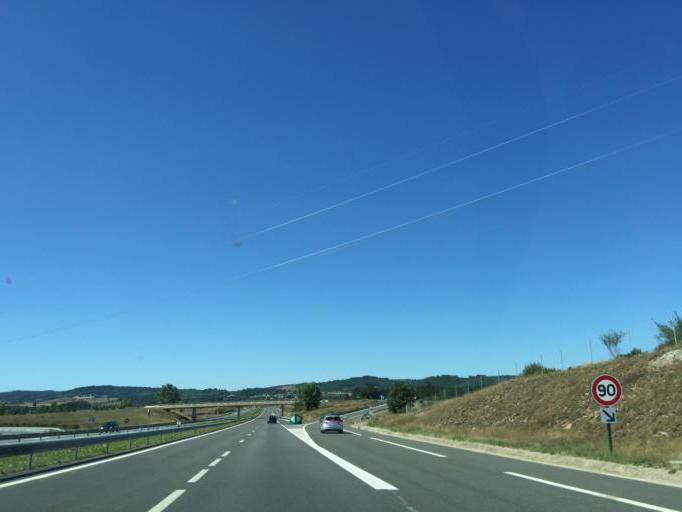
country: FR
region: Midi-Pyrenees
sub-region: Departement de l'Aveyron
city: La Cavalerie
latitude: 43.9488
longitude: 3.2184
